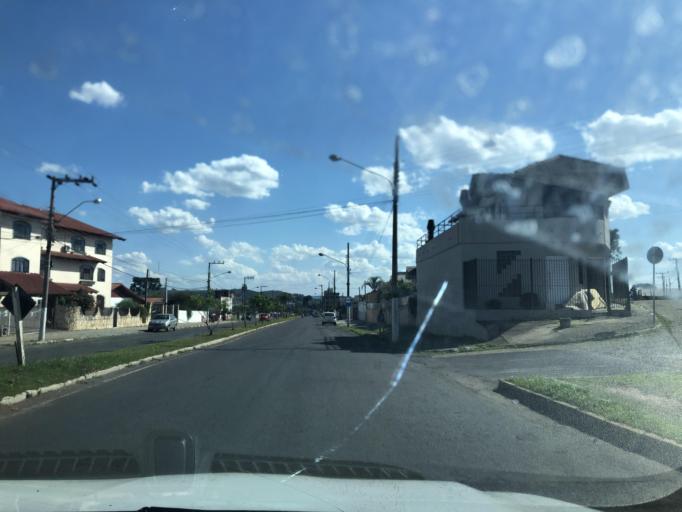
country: BR
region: Santa Catarina
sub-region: Lages
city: Lages
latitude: -27.8156
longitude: -50.3041
